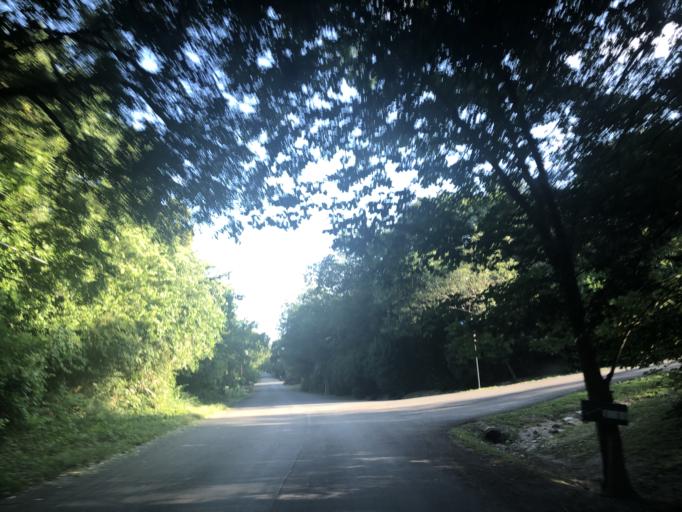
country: US
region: Texas
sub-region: Dallas County
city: Duncanville
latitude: 32.6722
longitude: -96.9222
